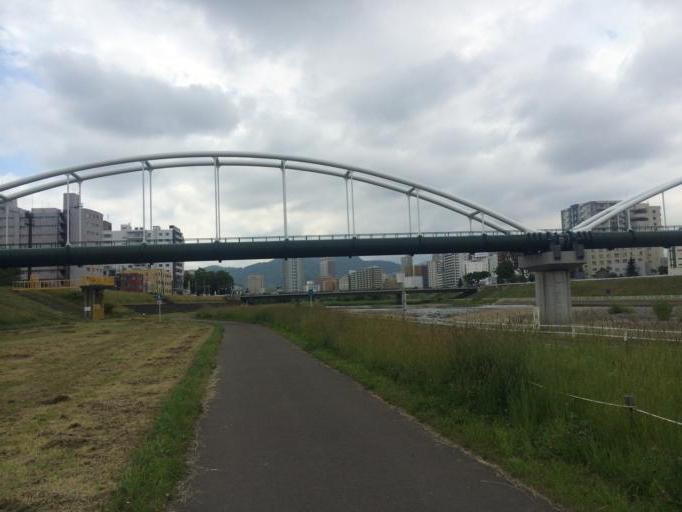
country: JP
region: Hokkaido
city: Sapporo
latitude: 43.0578
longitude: 141.3675
